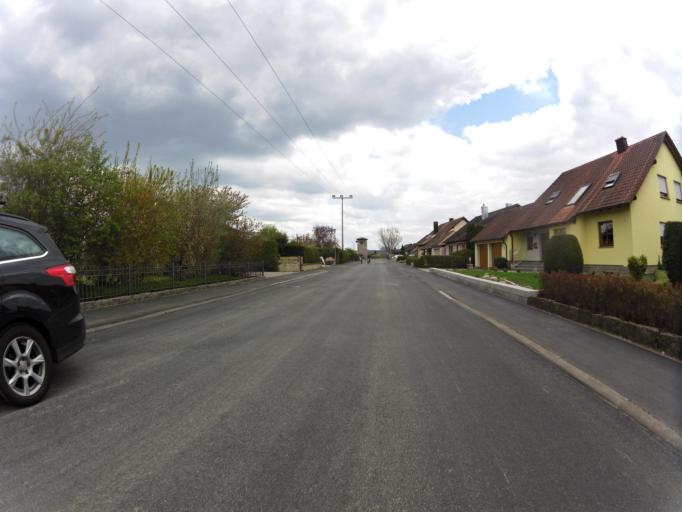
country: DE
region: Bavaria
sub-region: Regierungsbezirk Unterfranken
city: Giebelstadt
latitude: 49.6503
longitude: 9.9424
